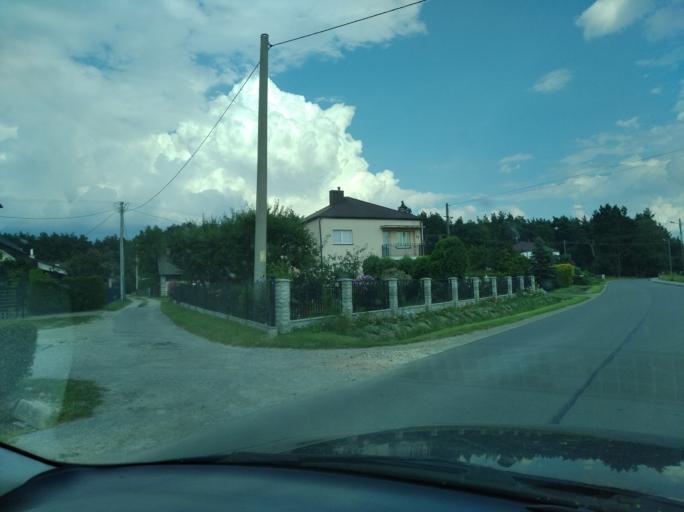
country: PL
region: Subcarpathian Voivodeship
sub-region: Powiat rzeszowski
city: Wysoka Glogowska
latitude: 50.1360
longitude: 22.0191
